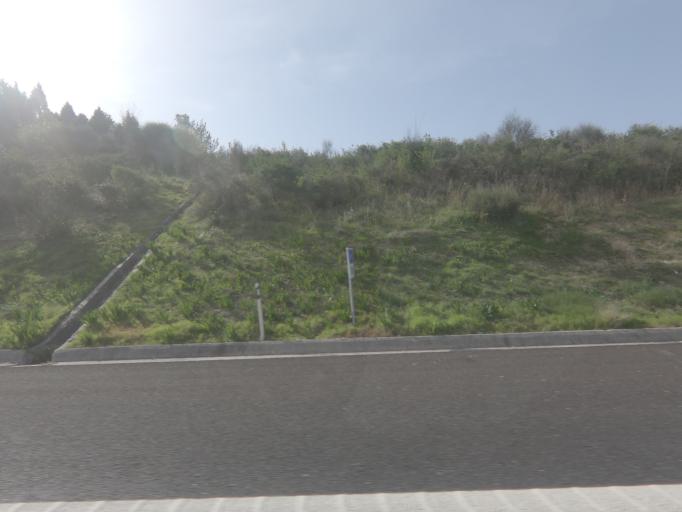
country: PT
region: Aveiro
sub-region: Mealhada
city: Mealhada
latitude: 40.3632
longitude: -8.4926
